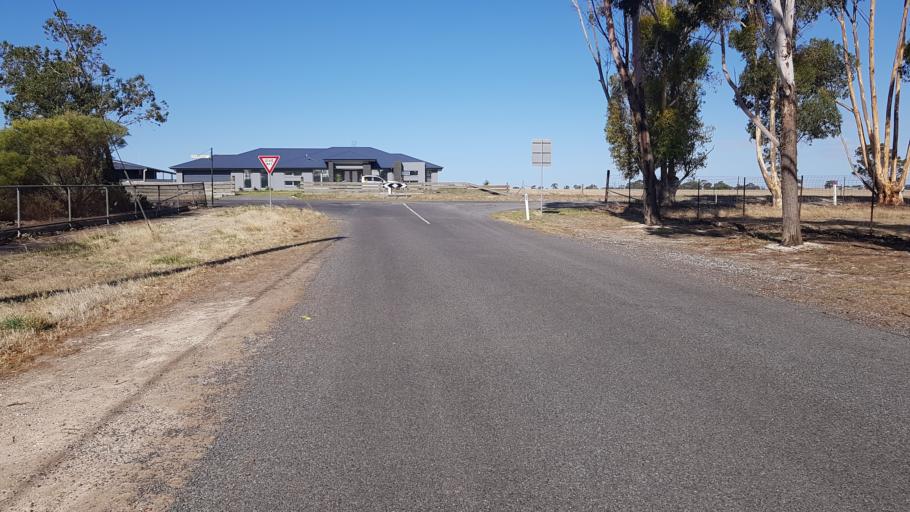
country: AU
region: Victoria
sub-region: Horsham
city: Horsham
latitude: -36.7418
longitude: 141.9504
